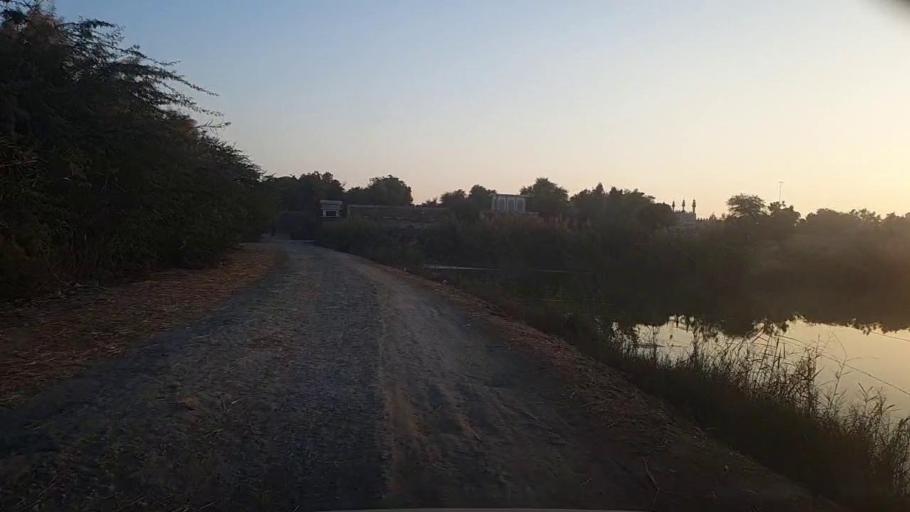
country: PK
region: Sindh
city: Khairpur Nathan Shah
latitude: 27.1565
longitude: 67.7318
